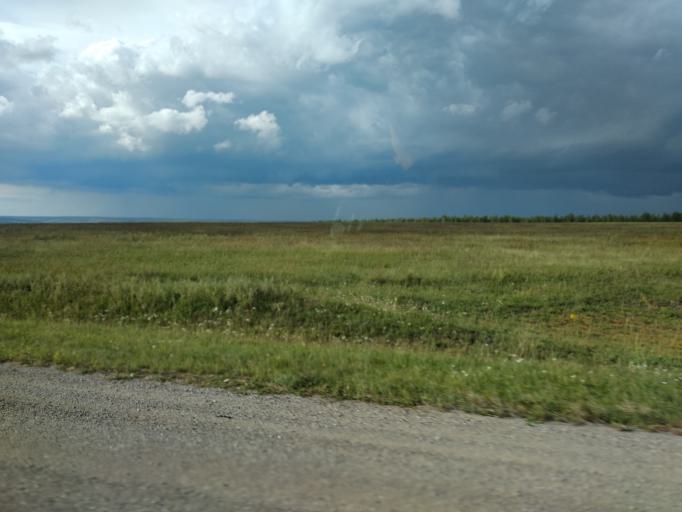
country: RU
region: Irkutsk
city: Bayanday
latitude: 52.9718
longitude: 105.3034
